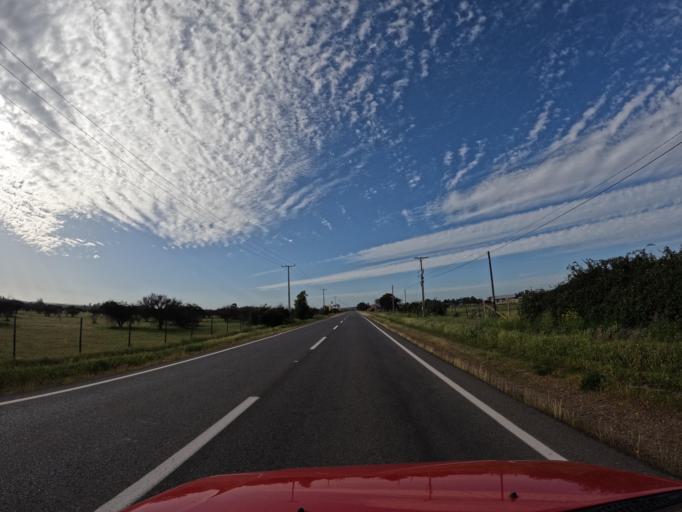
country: CL
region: Valparaiso
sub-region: San Antonio Province
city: San Antonio
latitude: -34.1588
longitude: -71.7322
